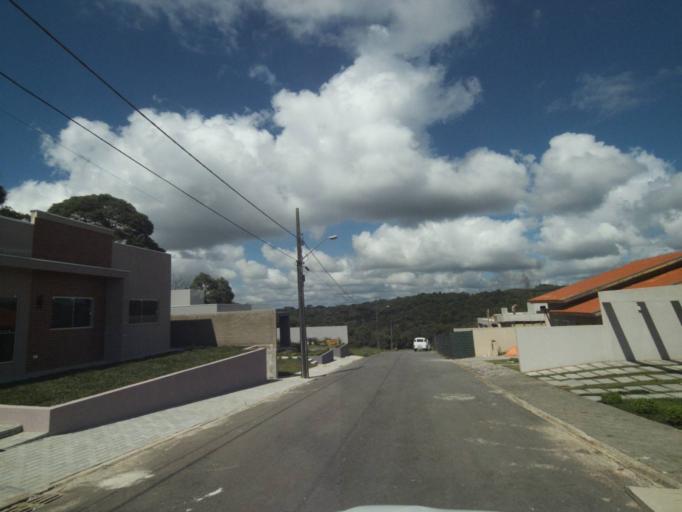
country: BR
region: Parana
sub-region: Colombo
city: Colombo
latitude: -25.3135
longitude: -49.2344
